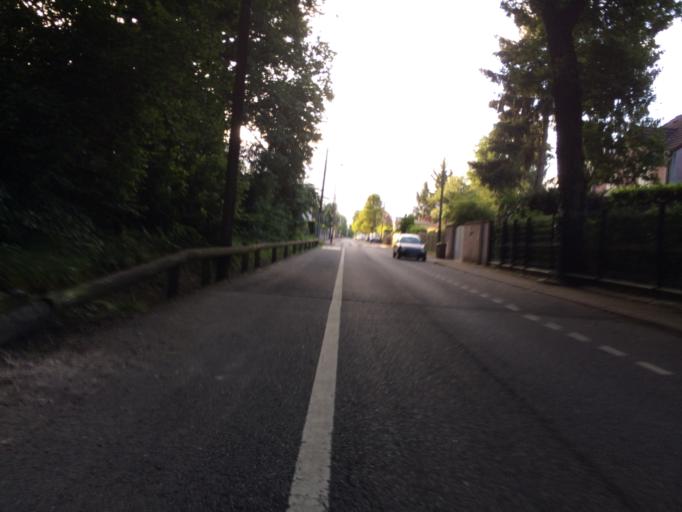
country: FR
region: Ile-de-France
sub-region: Departement de l'Essonne
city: Montgeron
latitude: 48.6920
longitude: 2.4668
